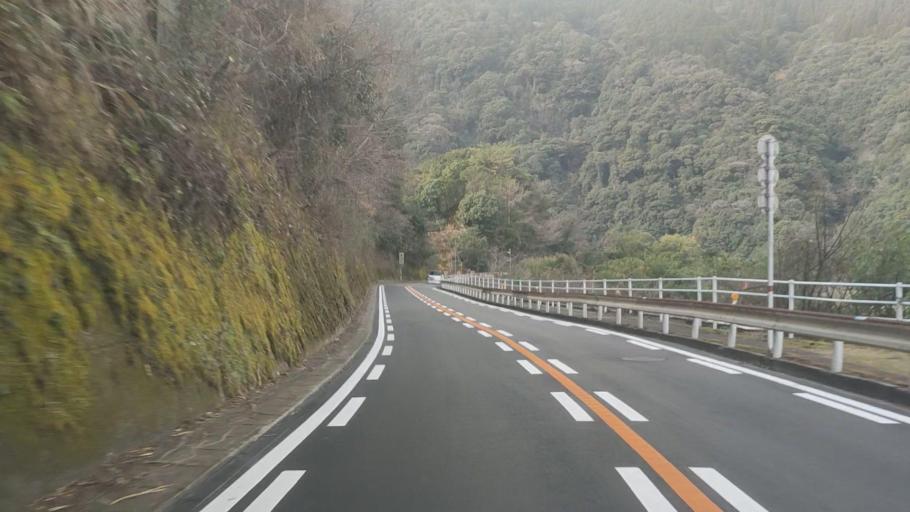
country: JP
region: Kumamoto
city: Hitoyoshi
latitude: 32.3028
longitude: 130.8460
